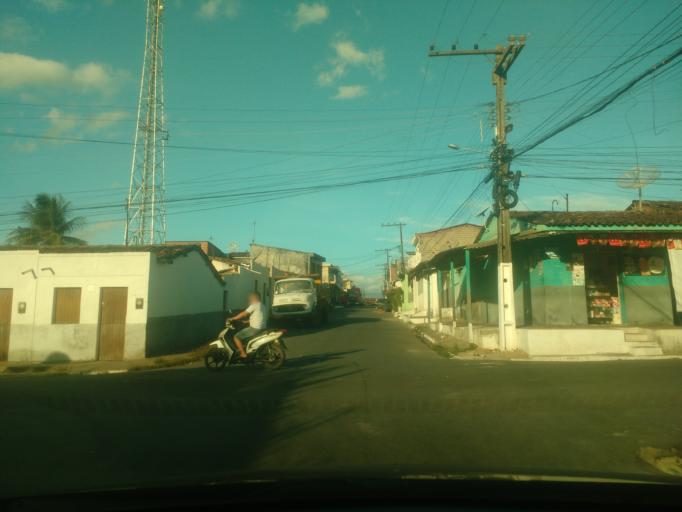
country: BR
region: Alagoas
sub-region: Uniao Dos Palmares
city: Uniao dos Palmares
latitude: -9.1617
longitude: -36.0280
